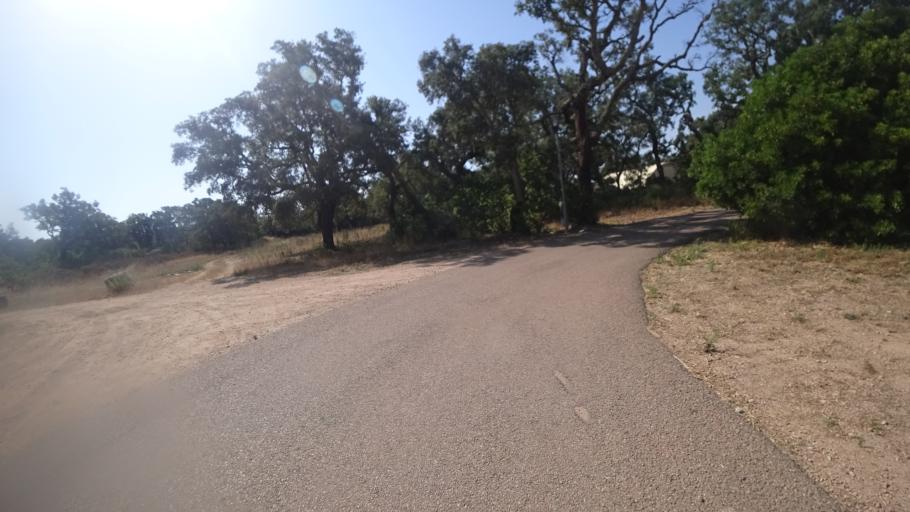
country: FR
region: Corsica
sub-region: Departement de la Corse-du-Sud
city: Porto-Vecchio
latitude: 41.6518
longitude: 9.3300
